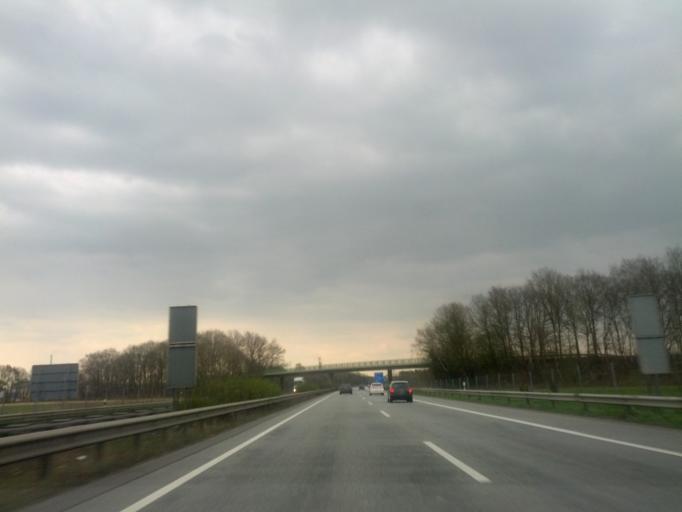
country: DE
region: Lower Saxony
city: Achim
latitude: 53.0212
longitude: 9.0518
